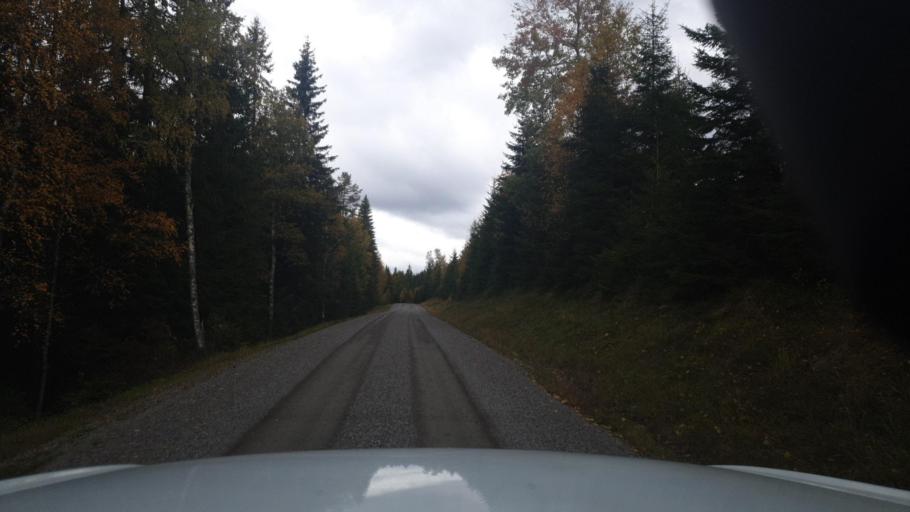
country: SE
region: Vaermland
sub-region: Eda Kommun
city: Charlottenberg
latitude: 60.0876
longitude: 12.6171
